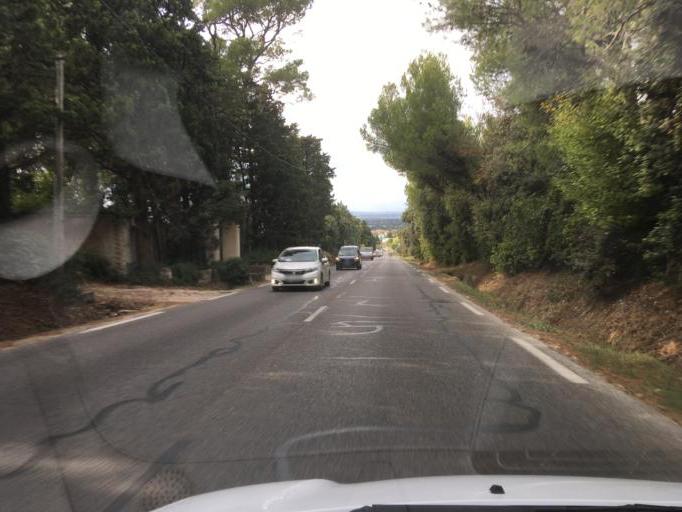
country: FR
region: Provence-Alpes-Cote d'Azur
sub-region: Departement du Vaucluse
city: Jonquerettes
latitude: 43.9358
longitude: 4.9189
